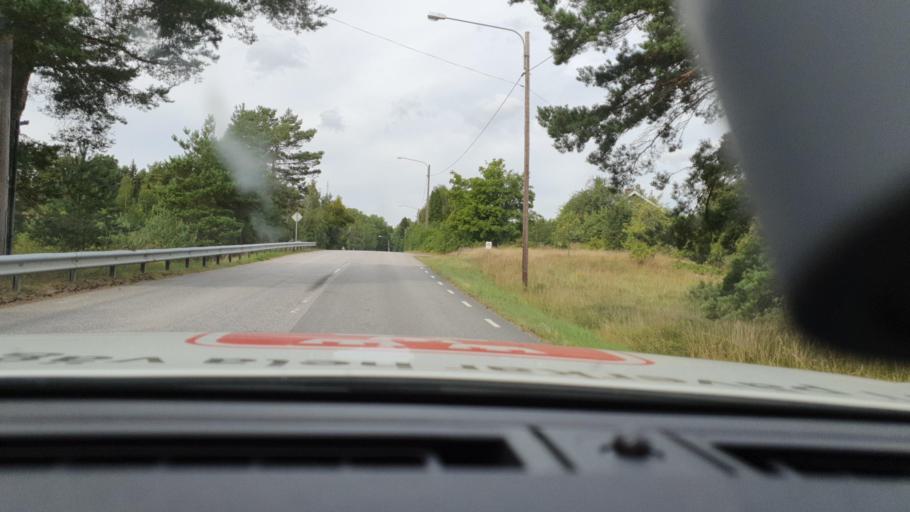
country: SE
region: Stockholm
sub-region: Norrtalje Kommun
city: Rimbo
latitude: 59.7271
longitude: 18.4938
